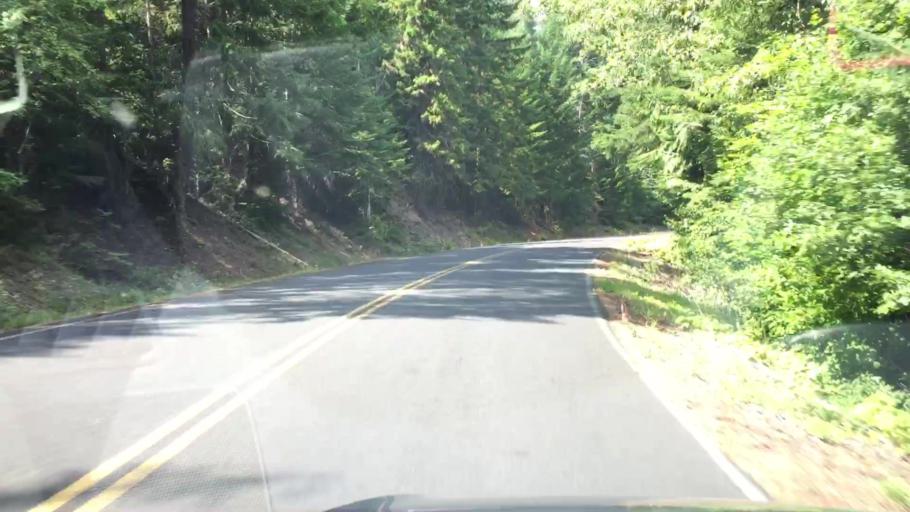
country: US
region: Washington
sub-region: Klickitat County
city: White Salmon
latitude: 46.0817
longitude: -121.5955
